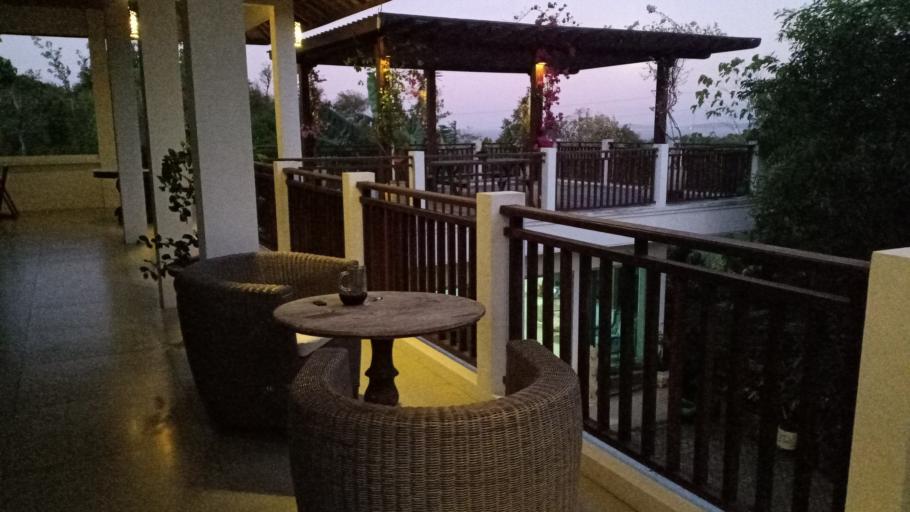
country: ID
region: East Java
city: Bangsring
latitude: -8.0657
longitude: 114.4128
